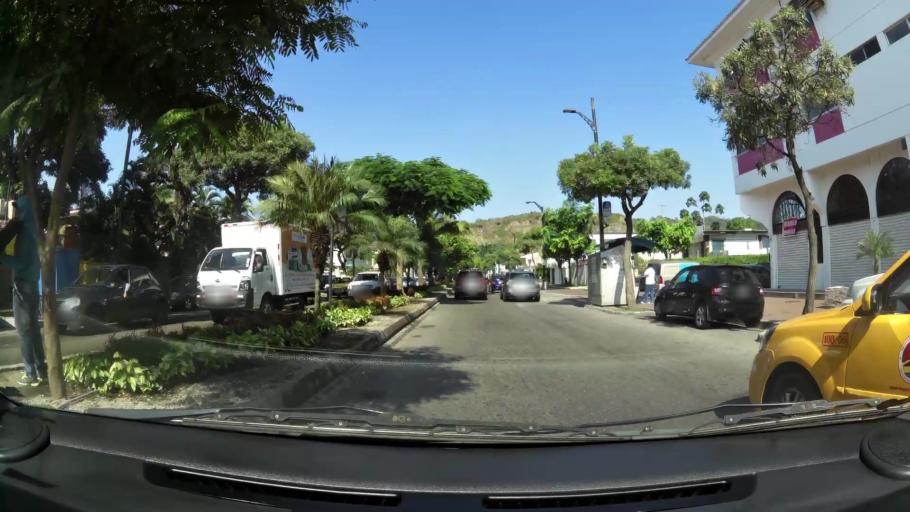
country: EC
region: Guayas
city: Guayaquil
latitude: -2.1700
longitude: -79.9101
